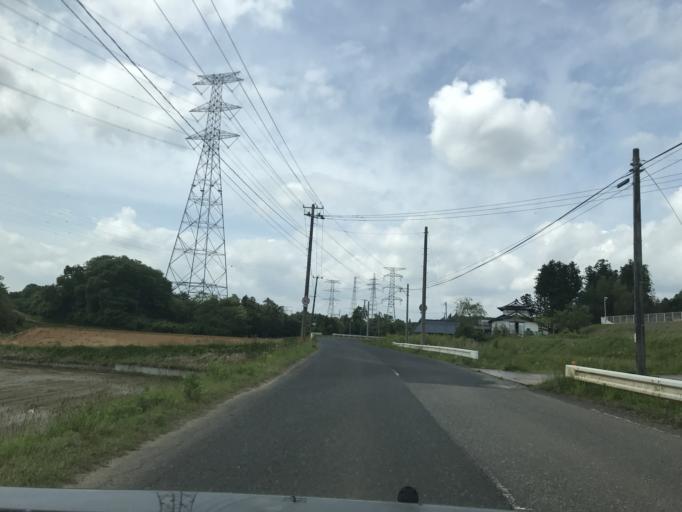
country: JP
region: Iwate
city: Ichinoseki
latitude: 38.8104
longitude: 141.0192
